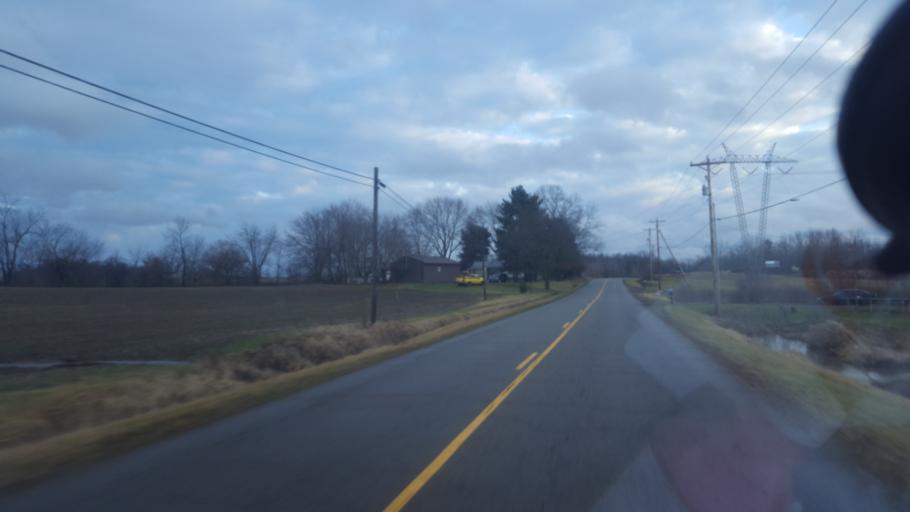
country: US
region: Ohio
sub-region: Knox County
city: Fredericktown
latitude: 40.5008
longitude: -82.5467
